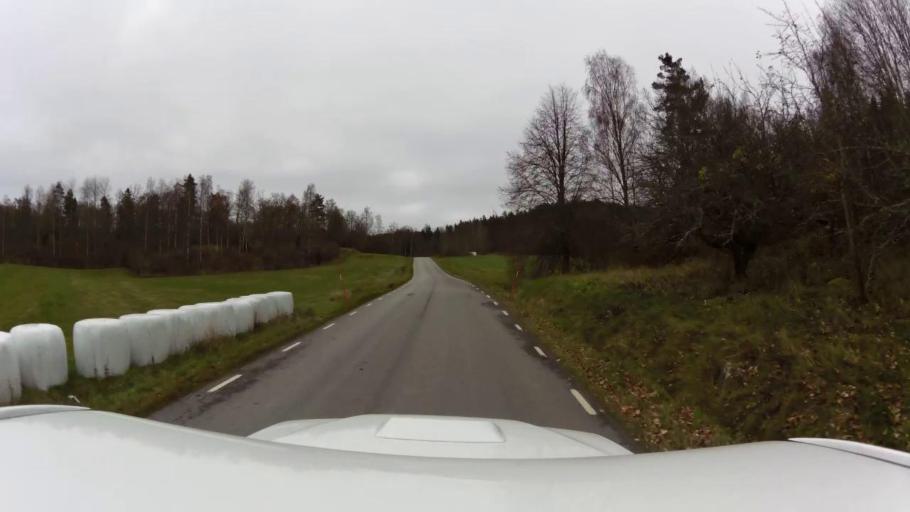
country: SE
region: OEstergoetland
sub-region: Kinda Kommun
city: Rimforsa
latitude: 58.1428
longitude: 15.6421
